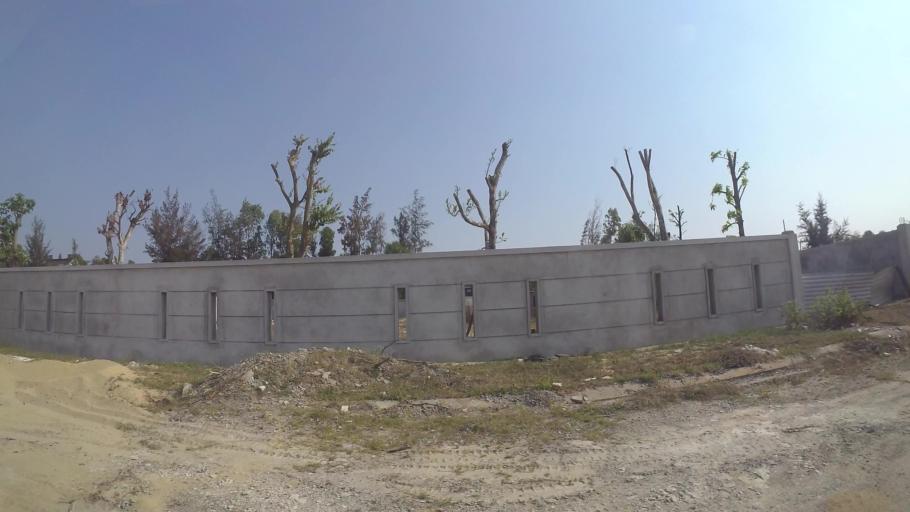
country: VN
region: Da Nang
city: Ngu Hanh Son
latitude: 15.9531
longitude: 108.2754
